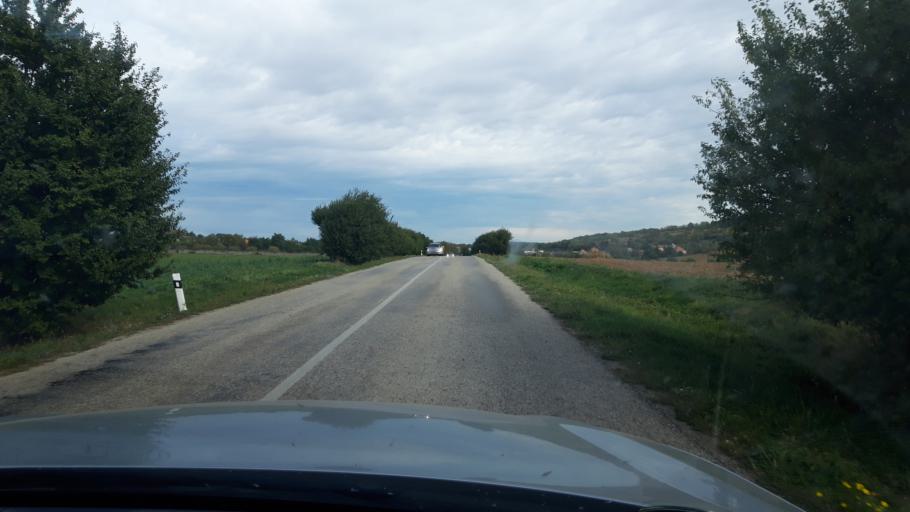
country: SK
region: Nitriansky
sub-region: Okres Nitra
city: Vrable
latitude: 48.1251
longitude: 18.3342
